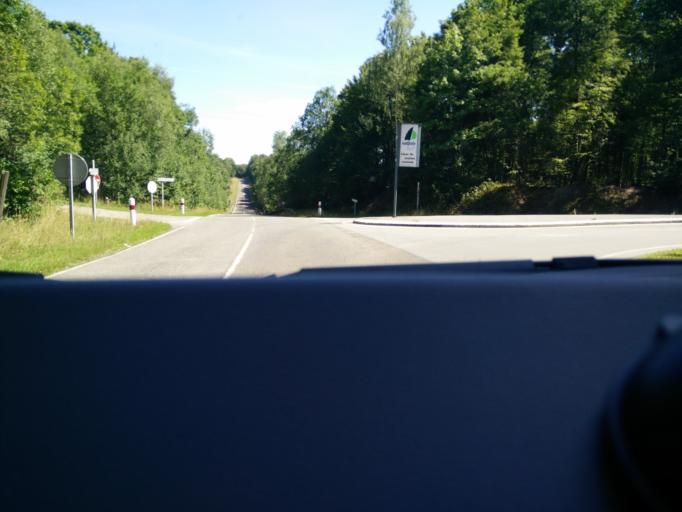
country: FR
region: Nord-Pas-de-Calais
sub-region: Departement du Nord
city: Trelon
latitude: 50.1216
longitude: 4.1415
